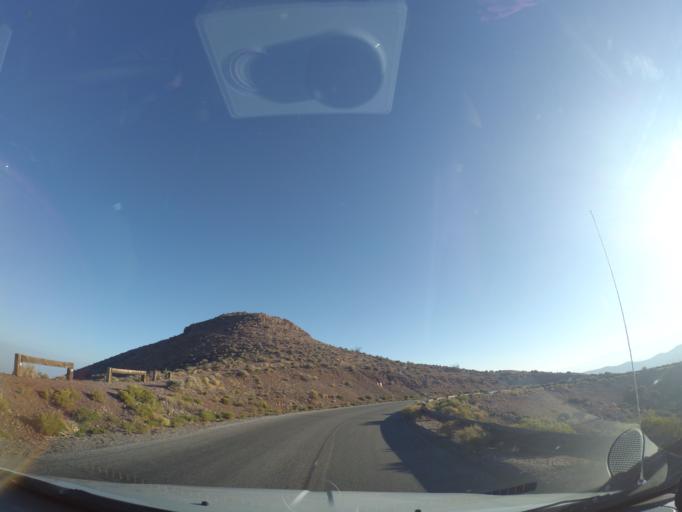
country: US
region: Nevada
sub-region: Nye County
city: Beatty
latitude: 36.2216
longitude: -116.7263
